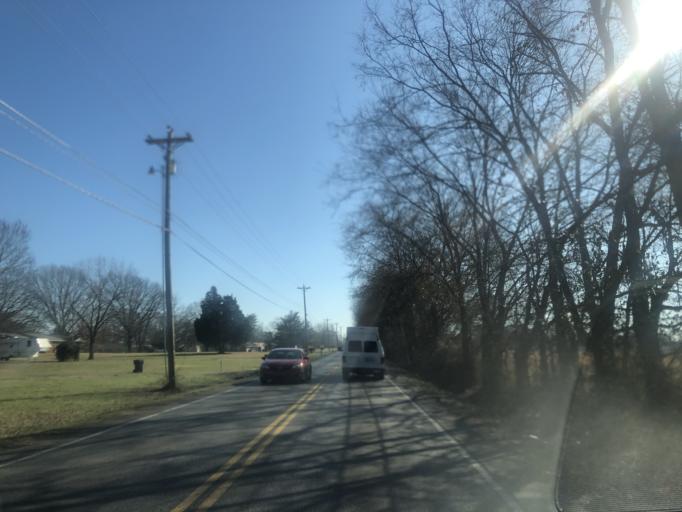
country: US
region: Tennessee
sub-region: Rutherford County
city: Smyrna
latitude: 35.9228
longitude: -86.4802
